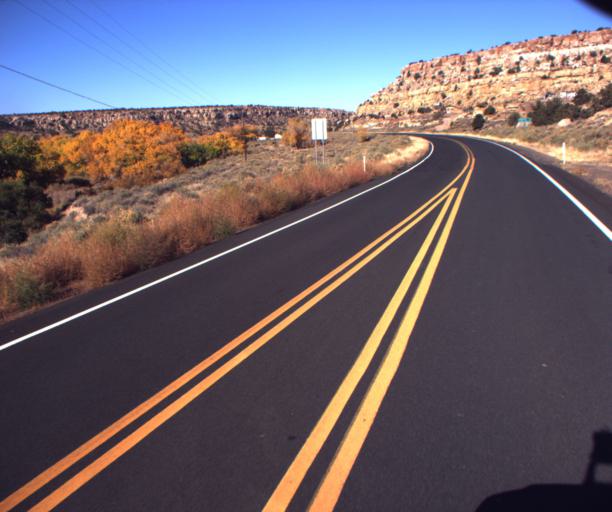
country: US
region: Arizona
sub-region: Navajo County
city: First Mesa
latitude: 35.8158
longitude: -110.2067
